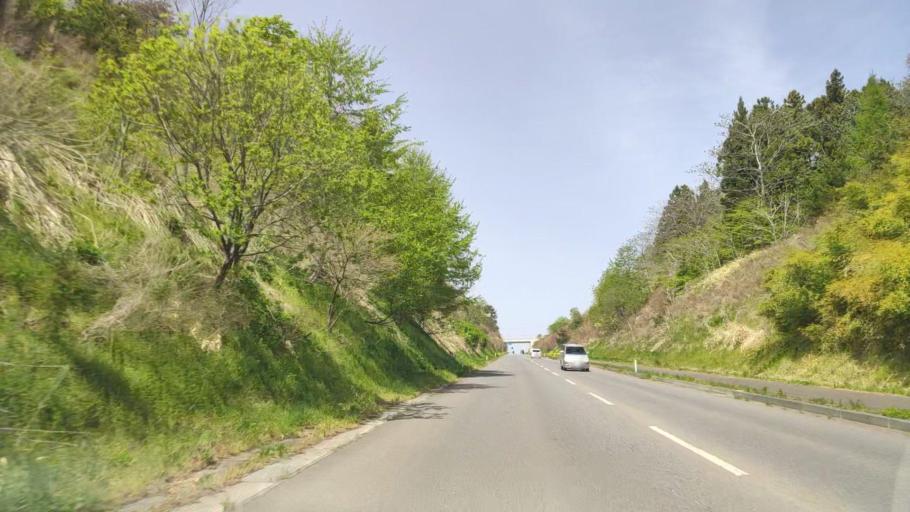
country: JP
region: Aomori
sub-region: Hachinohe Shi
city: Uchimaru
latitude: 40.5235
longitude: 141.4148
